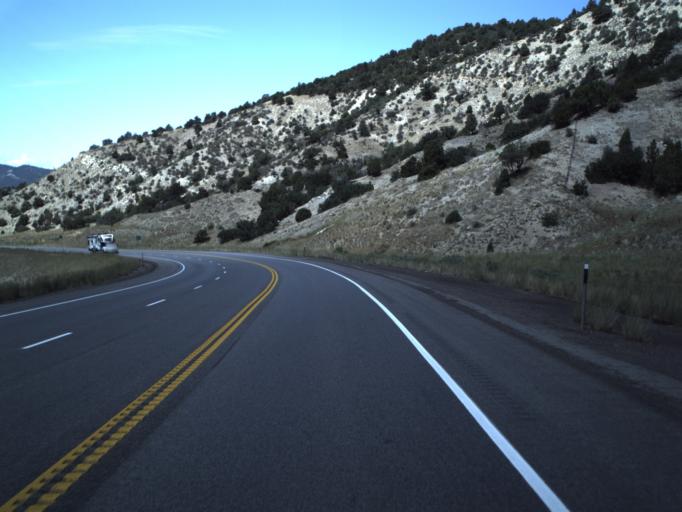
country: US
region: Utah
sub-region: Carbon County
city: Helper
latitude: 39.9336
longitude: -111.1557
